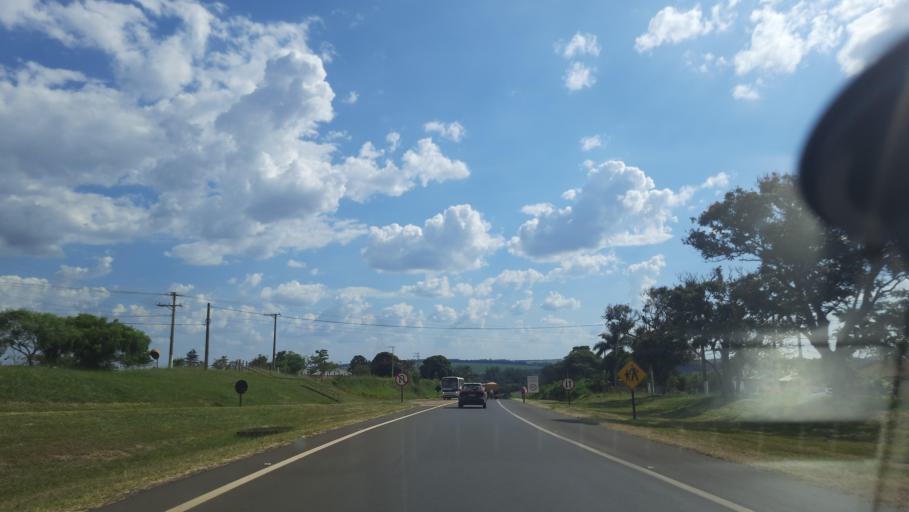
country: BR
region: Sao Paulo
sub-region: Casa Branca
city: Casa Branca
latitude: -21.7369
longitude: -46.9732
